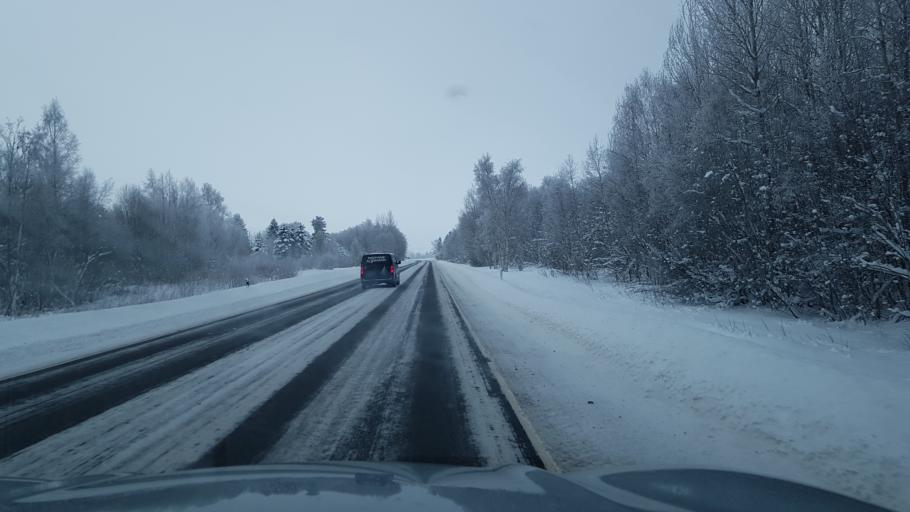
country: EE
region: Ida-Virumaa
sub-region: Johvi vald
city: Johvi
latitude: 59.2762
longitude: 27.3897
